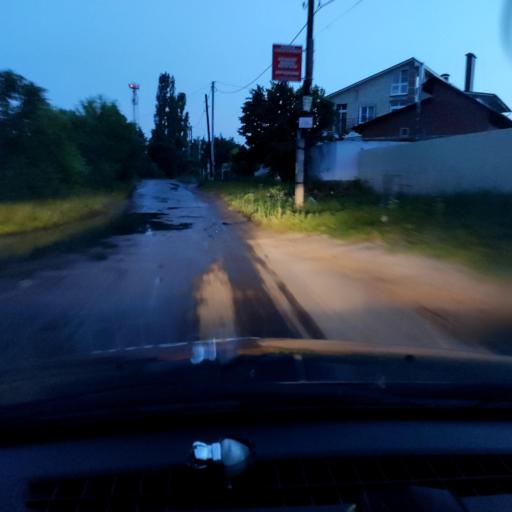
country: RU
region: Voronezj
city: Ramon'
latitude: 51.8298
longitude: 39.2707
